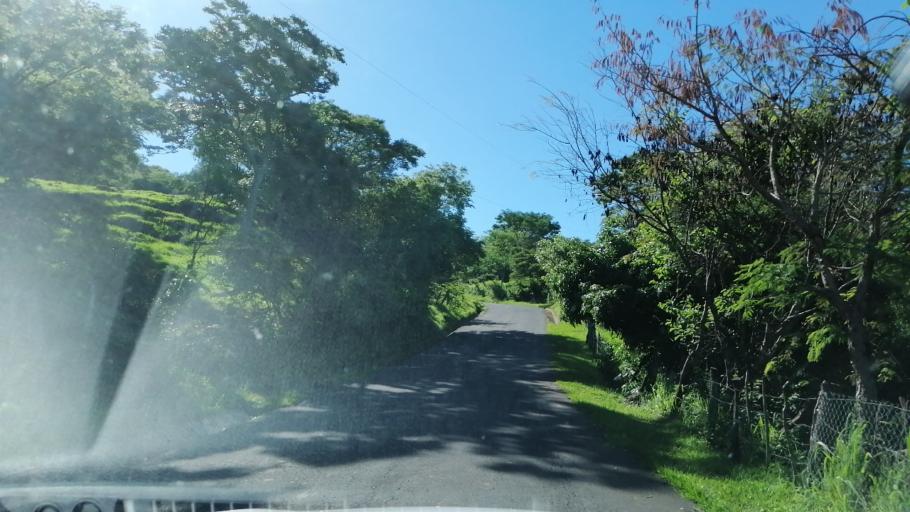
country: SV
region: Morazan
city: Corinto
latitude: 13.8114
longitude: -87.9975
